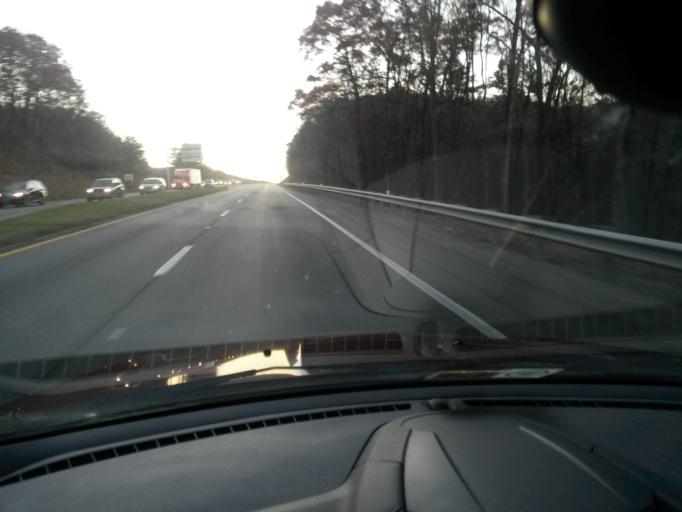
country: US
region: Virginia
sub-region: Roanoke County
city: Narrows
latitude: 37.2176
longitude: -79.9636
